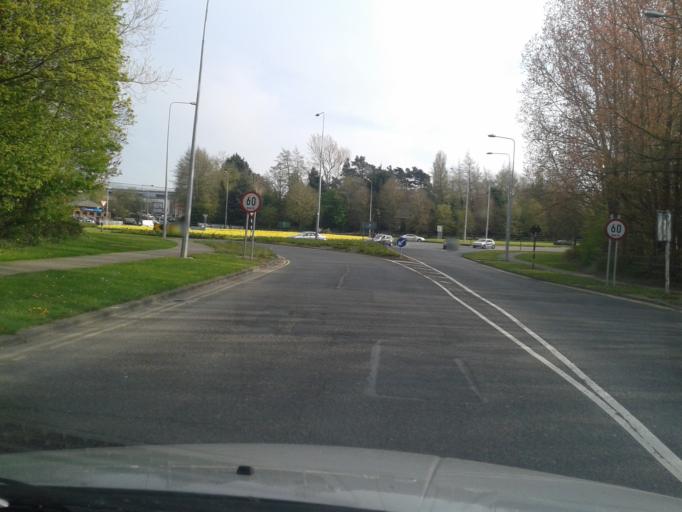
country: IE
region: Leinster
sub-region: Fingal County
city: Swords
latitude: 53.4507
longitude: -6.2252
